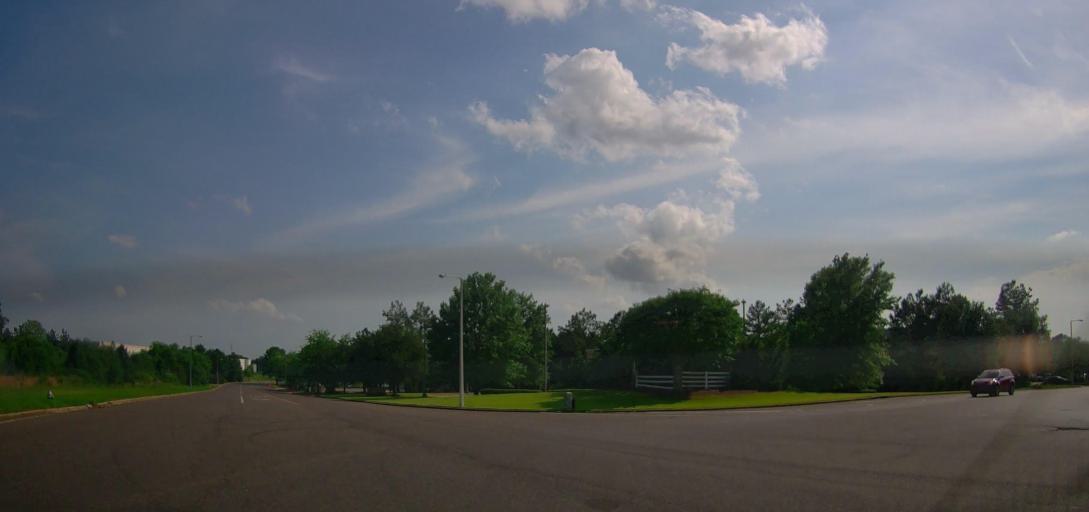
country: US
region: Mississippi
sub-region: De Soto County
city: Olive Branch
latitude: 35.0028
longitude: -89.8575
